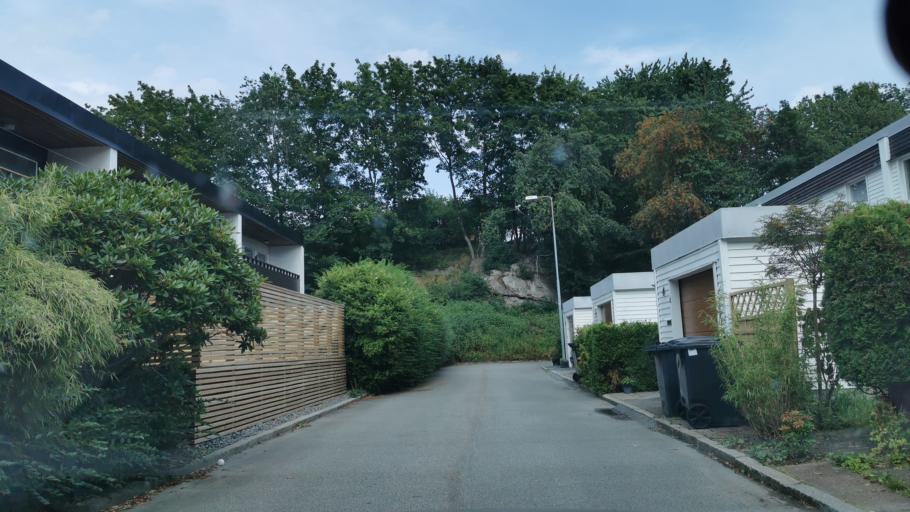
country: SE
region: Vaestra Goetaland
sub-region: Molndal
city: Moelndal
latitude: 57.6679
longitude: 11.9822
